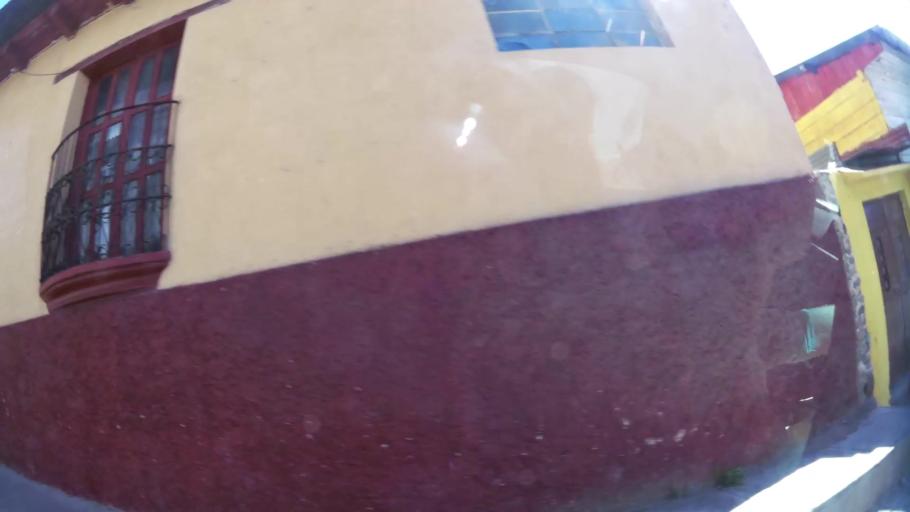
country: GT
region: Solola
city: Solola
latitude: 14.7750
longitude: -91.1821
